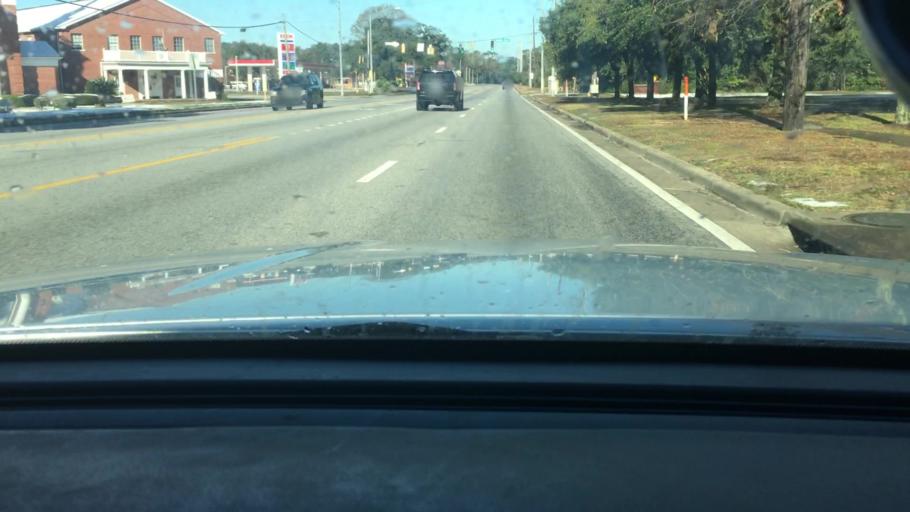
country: US
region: Alabama
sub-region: Mobile County
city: Prichard
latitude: 30.7265
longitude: -88.1696
